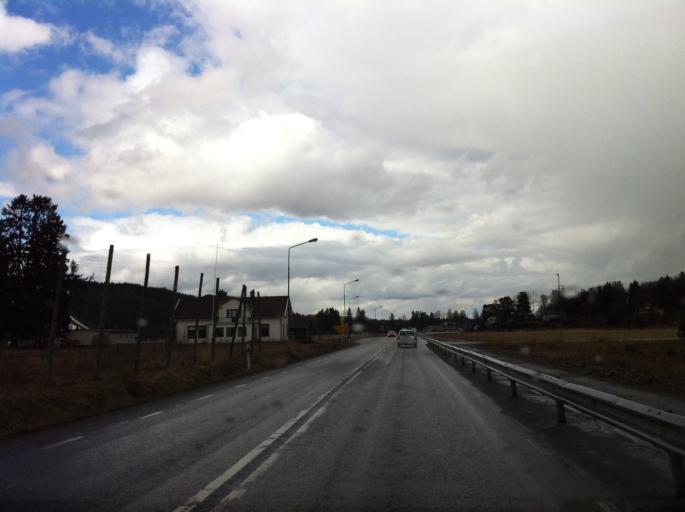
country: SE
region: Vaestra Goetaland
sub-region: Ulricehamns Kommun
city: Ulricehamn
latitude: 57.7448
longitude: 13.4258
